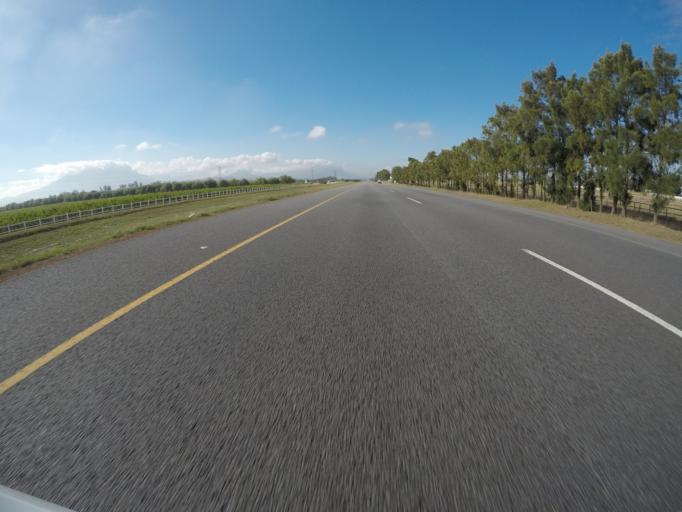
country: ZA
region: Western Cape
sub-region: City of Cape Town
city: Kraaifontein
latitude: -33.8455
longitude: 18.8027
